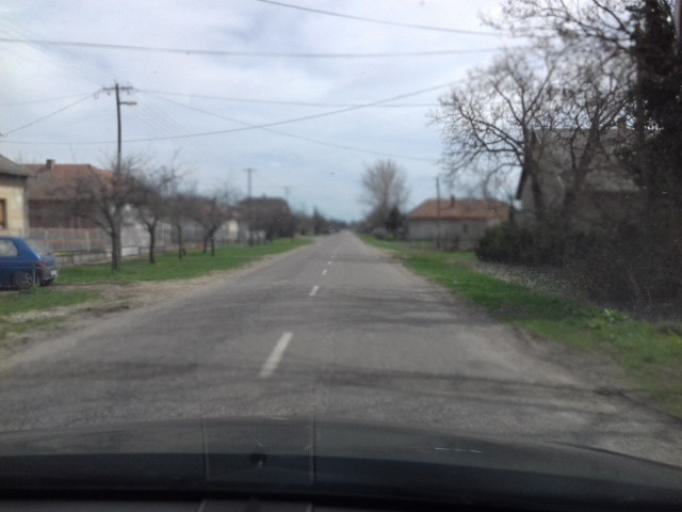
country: HU
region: Jasz-Nagykun-Szolnok
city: Cserkeszolo
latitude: 46.9049
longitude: 20.1572
